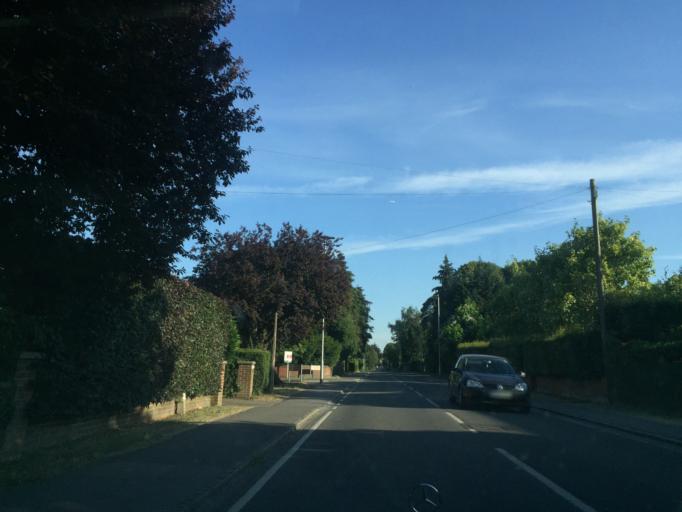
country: GB
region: England
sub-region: Wokingham
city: Twyford
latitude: 51.4846
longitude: -0.8694
